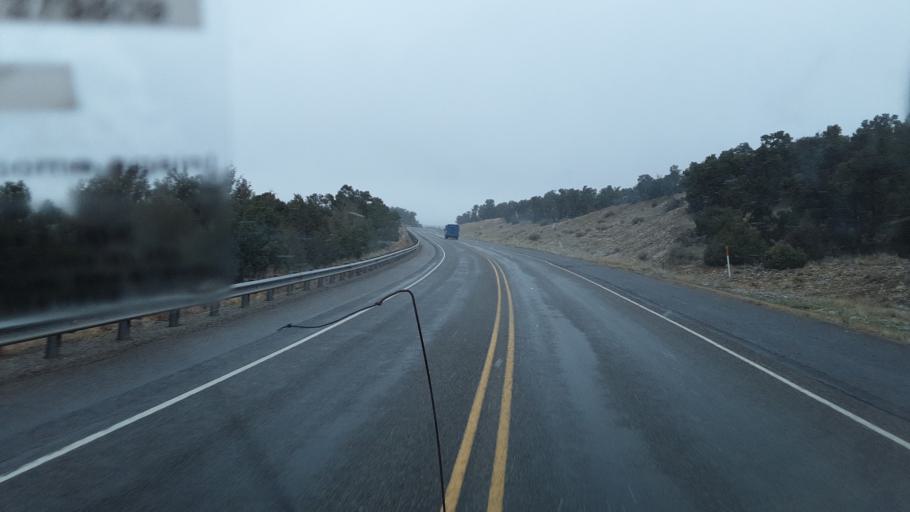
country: US
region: New Mexico
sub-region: Rio Arriba County
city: Tierra Amarilla
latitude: 36.4726
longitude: -106.4886
